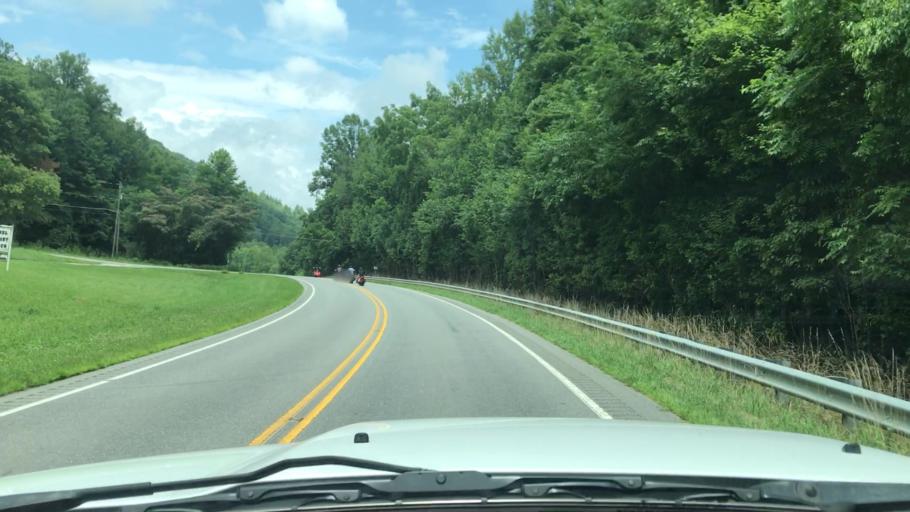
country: US
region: North Carolina
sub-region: Graham County
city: Robbinsville
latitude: 35.2737
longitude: -83.7553
